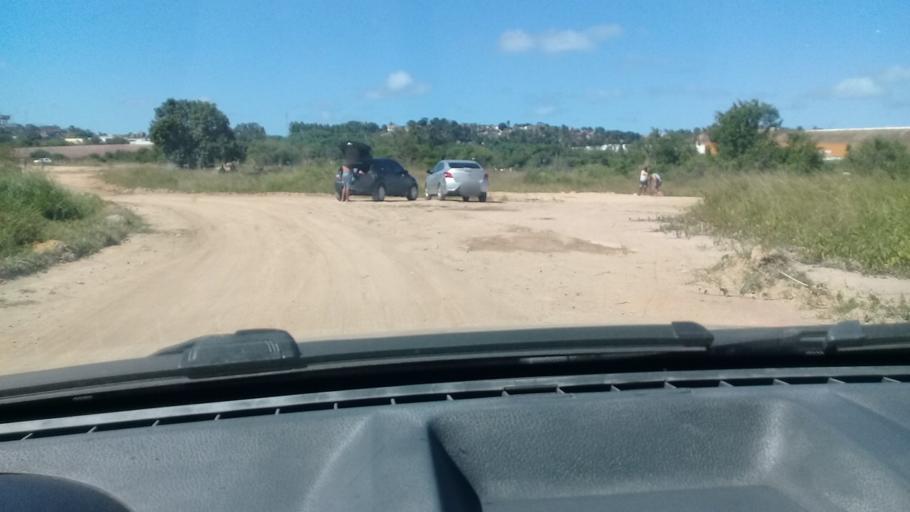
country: BR
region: Pernambuco
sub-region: Jaboatao Dos Guararapes
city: Jaboatao
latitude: -8.1483
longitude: -34.9505
